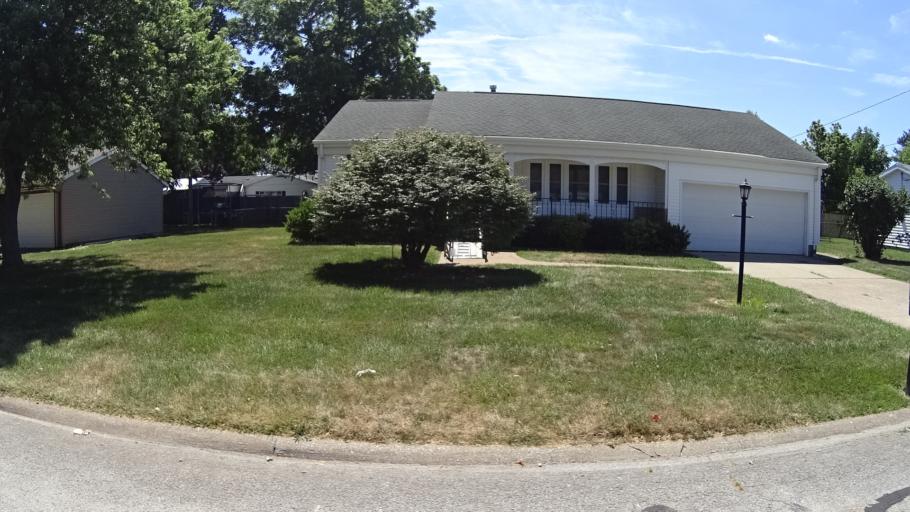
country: US
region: Ohio
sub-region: Erie County
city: Sandusky
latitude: 41.4122
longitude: -82.6914
